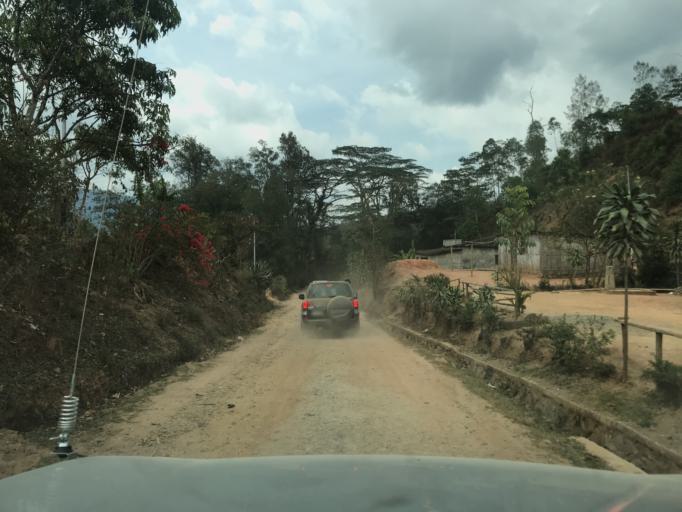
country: TL
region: Ermera
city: Gleno
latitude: -8.8201
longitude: 125.4324
